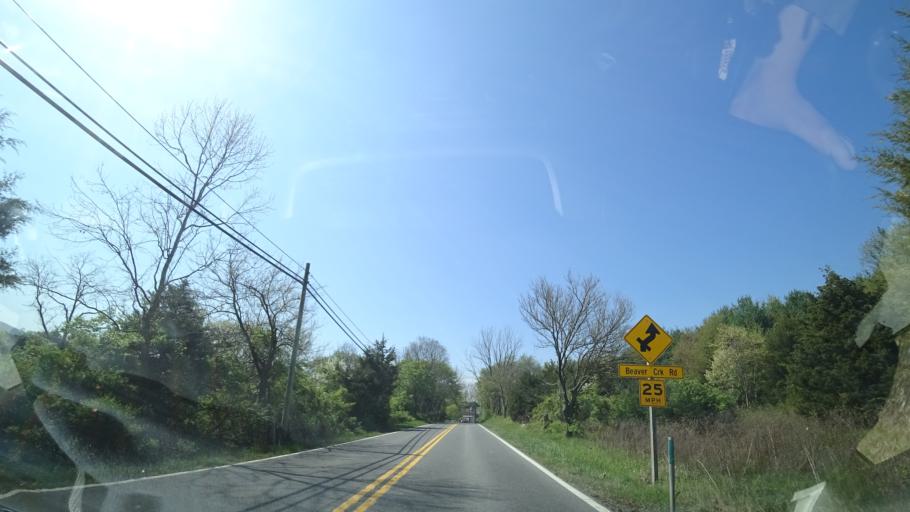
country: US
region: Maryland
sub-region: Washington County
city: Robinwood
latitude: 39.5760
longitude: -77.6458
